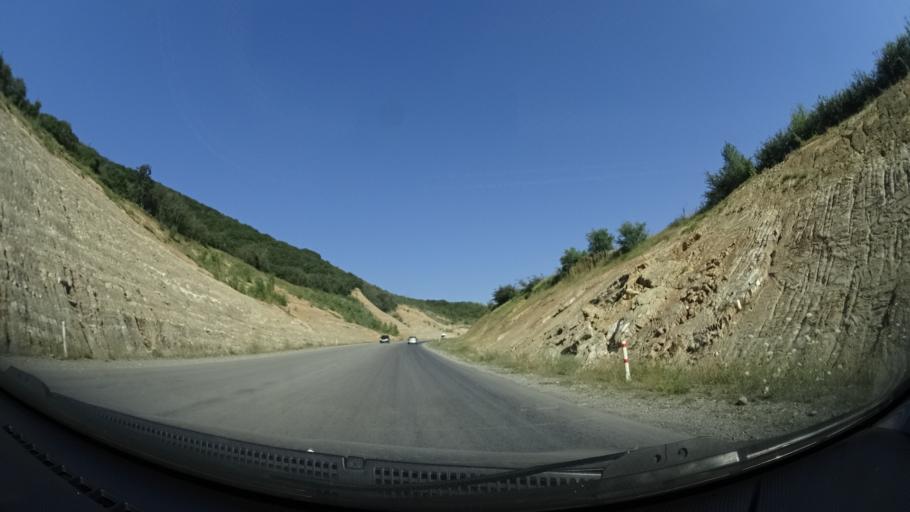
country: GE
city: Didi Lilo
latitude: 41.8032
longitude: 44.9105
